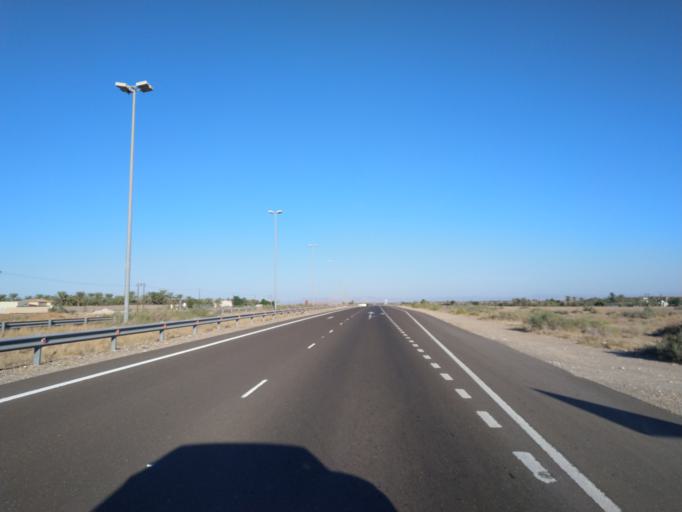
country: OM
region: Al Buraimi
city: Al Buraymi
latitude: 24.5411
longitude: 55.6365
